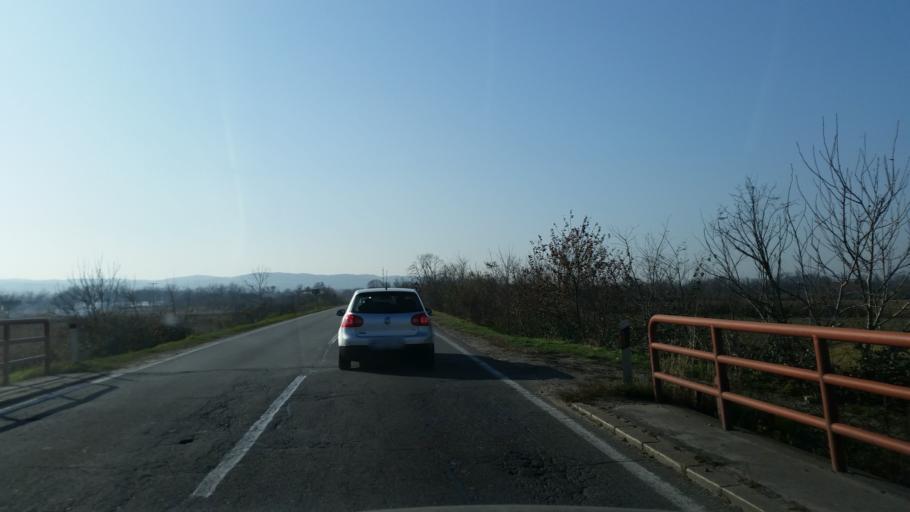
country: RS
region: Central Serbia
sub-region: Belgrade
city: Lazarevac
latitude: 44.3985
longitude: 20.2457
